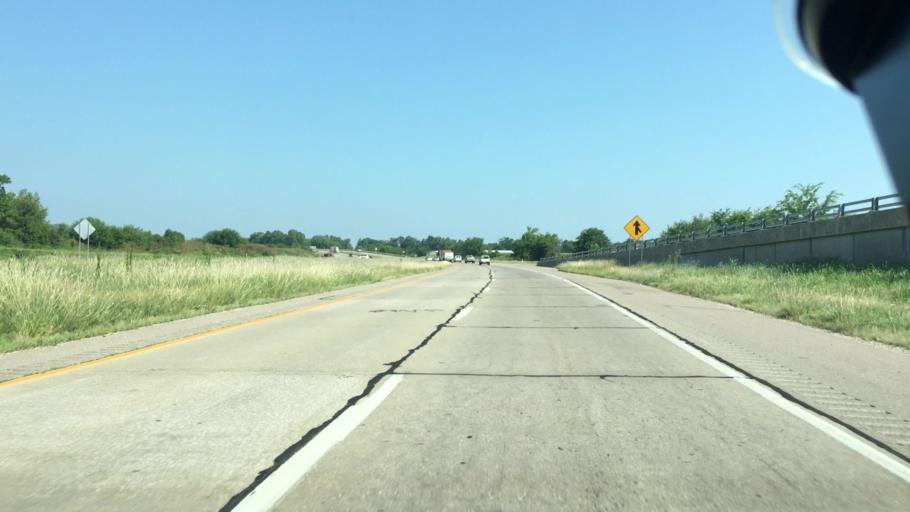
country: US
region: Indiana
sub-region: Gibson County
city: Princeton
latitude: 38.3136
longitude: -87.5690
